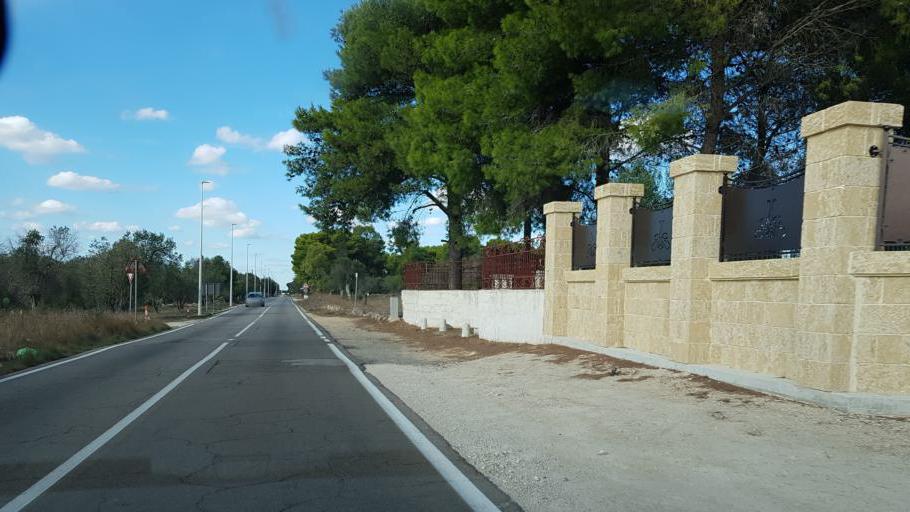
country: IT
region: Apulia
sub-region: Provincia di Lecce
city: Nardo
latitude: 40.1385
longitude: 18.0190
